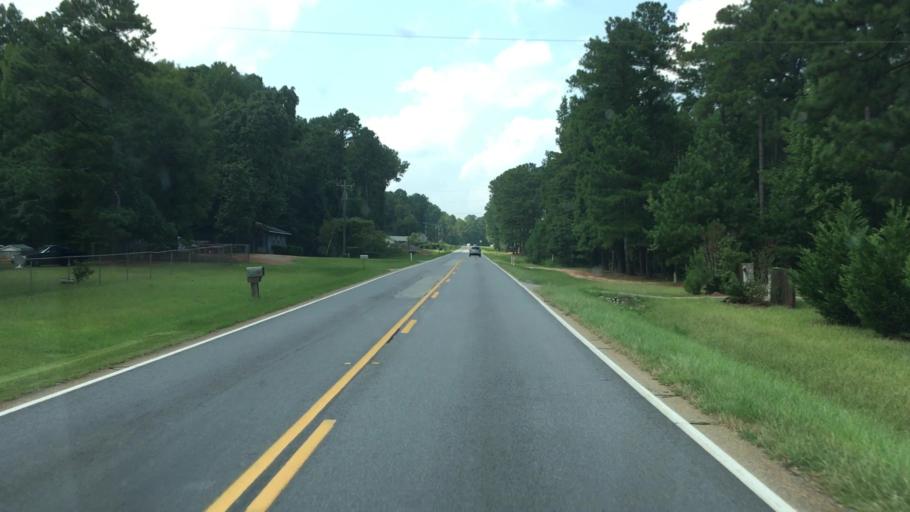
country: US
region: Georgia
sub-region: Jasper County
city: Monticello
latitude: 33.2623
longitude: -83.7181
